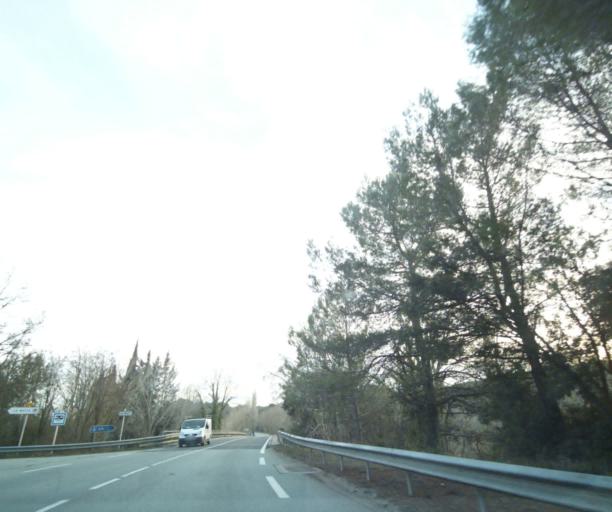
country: FR
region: Provence-Alpes-Cote d'Azur
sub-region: Departement du Var
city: La Motte
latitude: 43.4916
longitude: 6.5117
